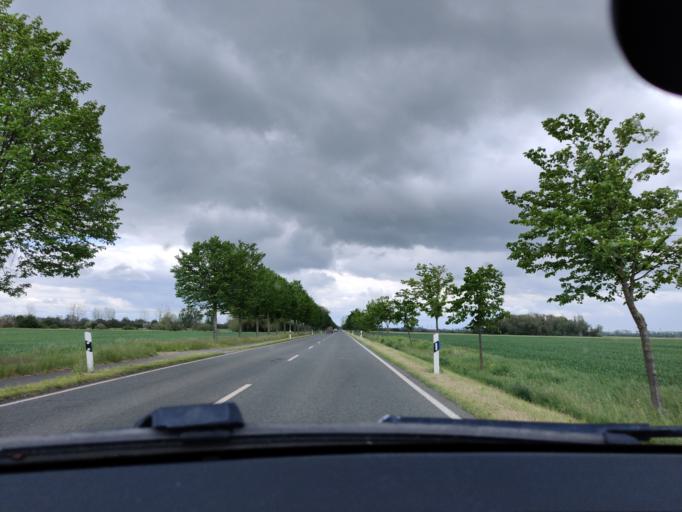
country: DE
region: Saxony-Anhalt
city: Barby
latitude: 51.9716
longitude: 11.8389
